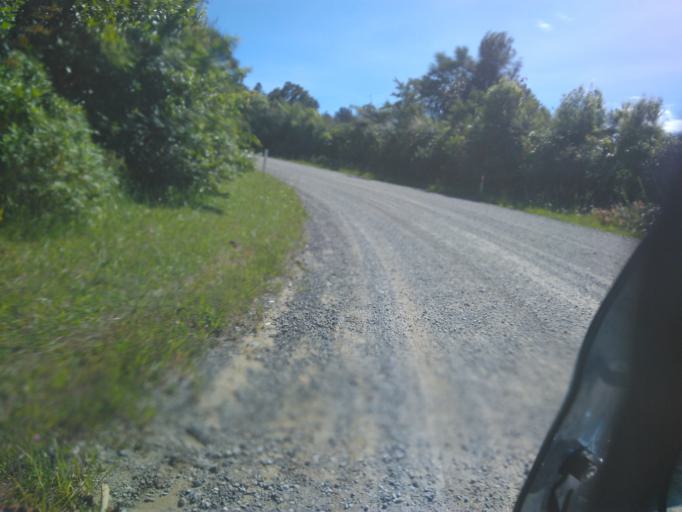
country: NZ
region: Hawke's Bay
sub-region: Wairoa District
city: Wairoa
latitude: -38.7987
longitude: 177.1246
